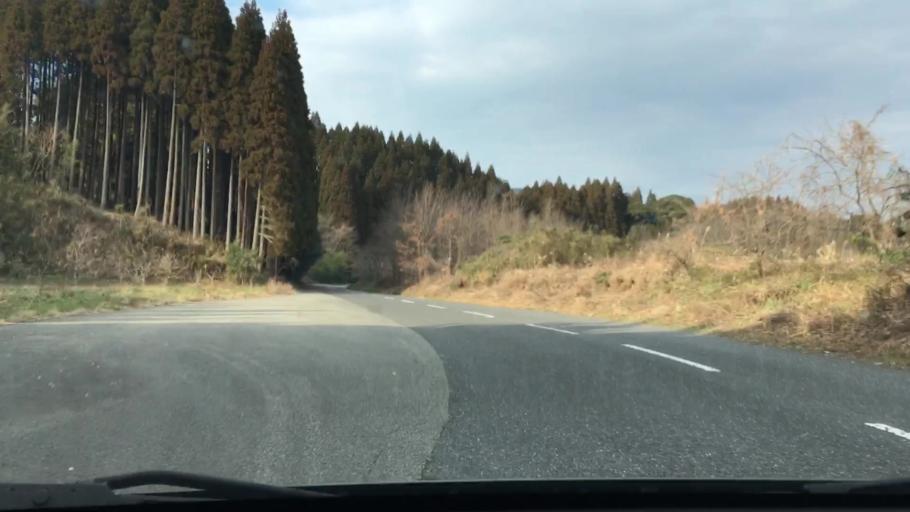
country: JP
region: Miyazaki
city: Nichinan
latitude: 31.6197
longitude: 131.3365
